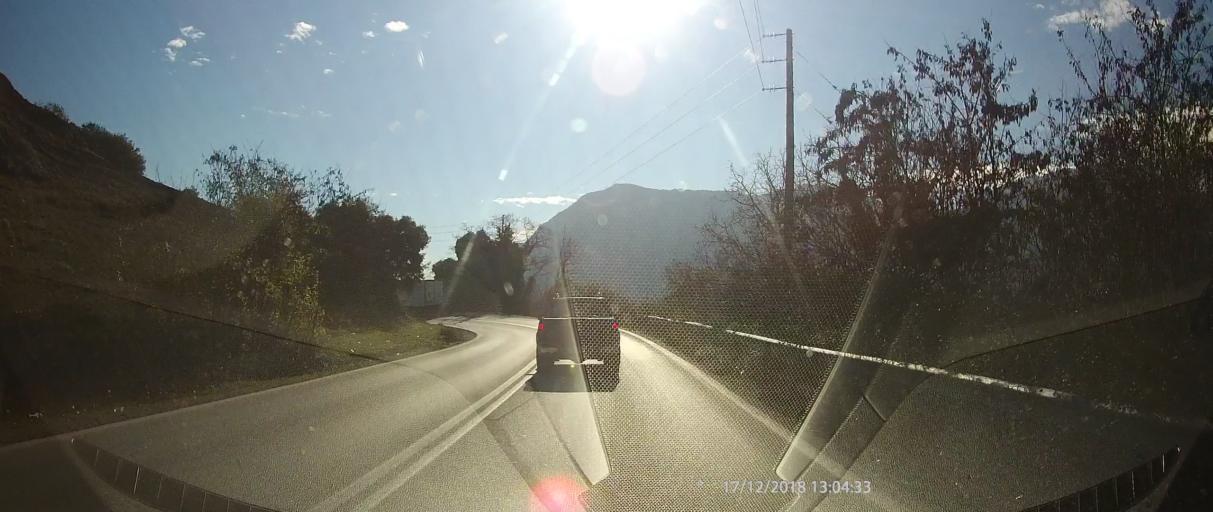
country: GR
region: Thessaly
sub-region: Trikala
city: Kastraki
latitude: 39.7042
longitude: 21.6115
